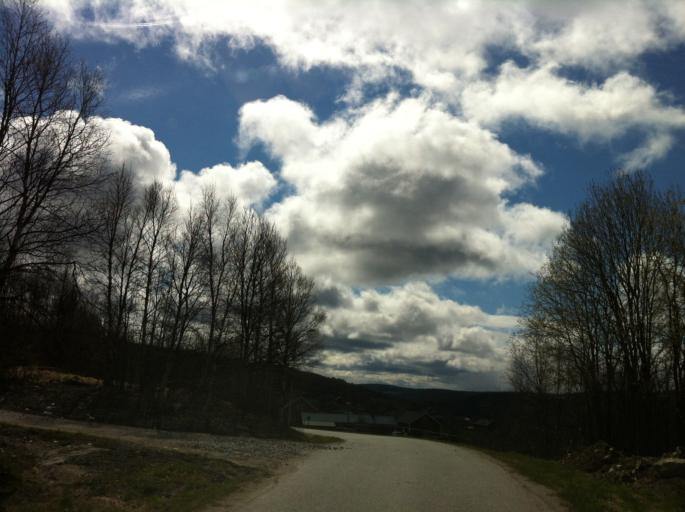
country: NO
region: Sor-Trondelag
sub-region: Tydal
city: Aas
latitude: 62.6443
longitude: 12.4404
